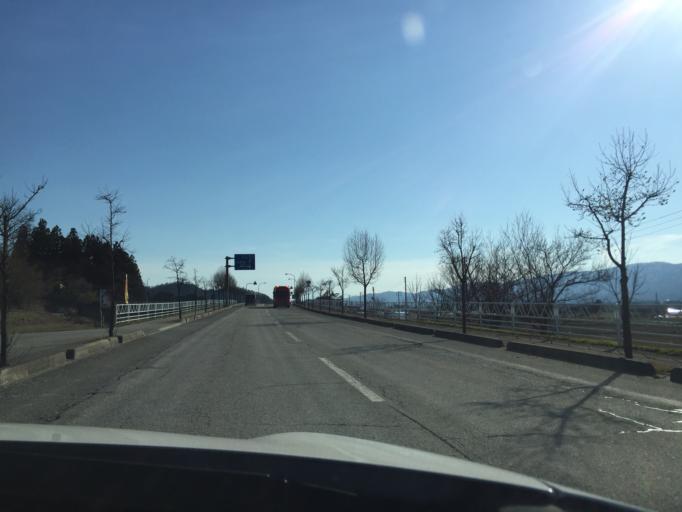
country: JP
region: Yamagata
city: Nagai
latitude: 38.1728
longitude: 140.0916
